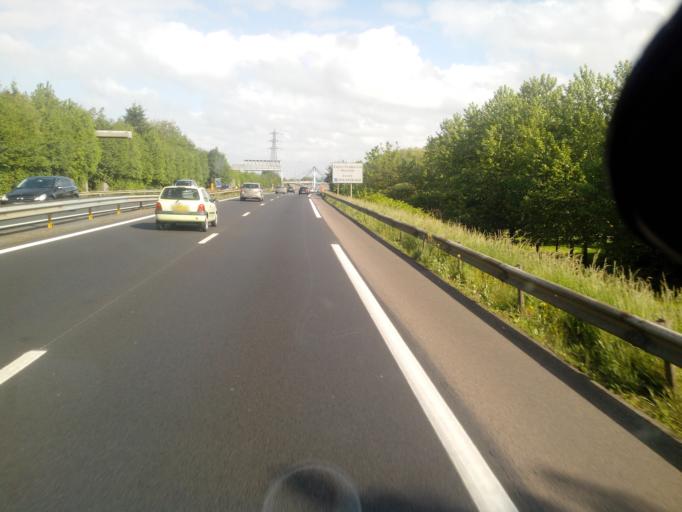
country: FR
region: Lower Normandy
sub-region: Departement du Calvados
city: Mondeville
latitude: 49.1752
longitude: -0.3127
